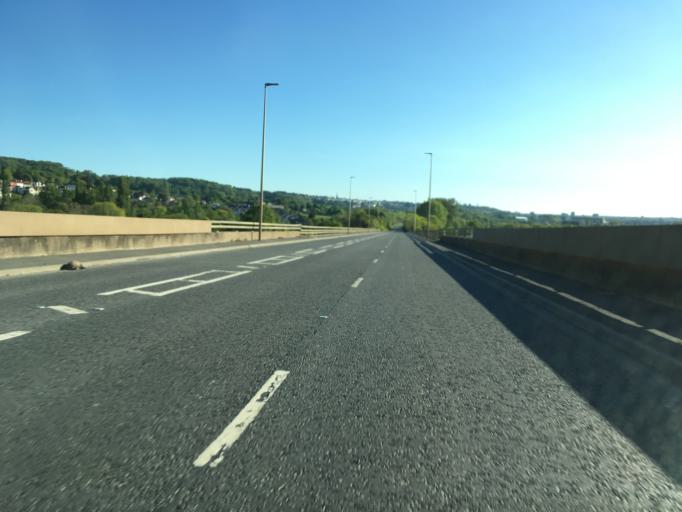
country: GB
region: England
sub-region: North Somerset
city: Long Ashton
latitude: 51.4270
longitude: -2.6505
